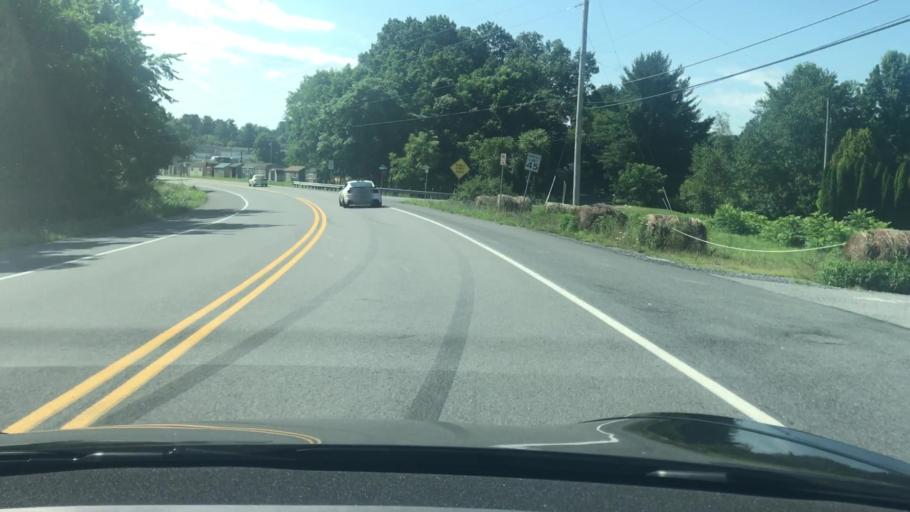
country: US
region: Pennsylvania
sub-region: York County
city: Valley Green
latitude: 40.1346
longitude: -76.8651
